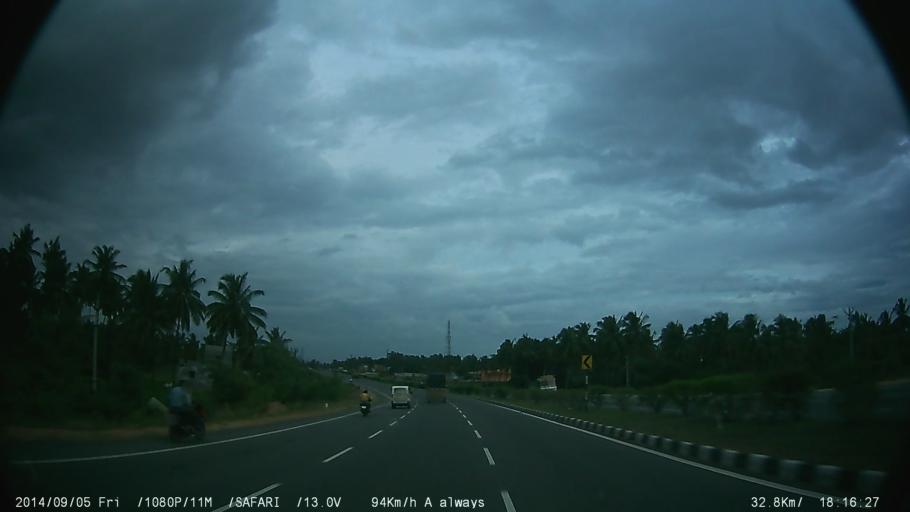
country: IN
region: Tamil Nadu
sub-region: Krishnagiri
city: Kelamangalam
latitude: 12.6745
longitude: 77.9692
